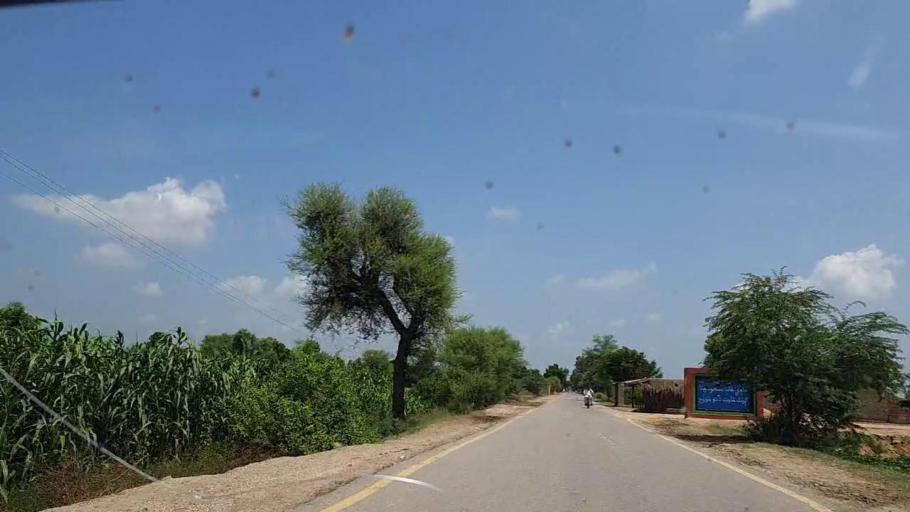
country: PK
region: Sindh
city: Tharu Shah
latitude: 26.9571
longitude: 68.1030
